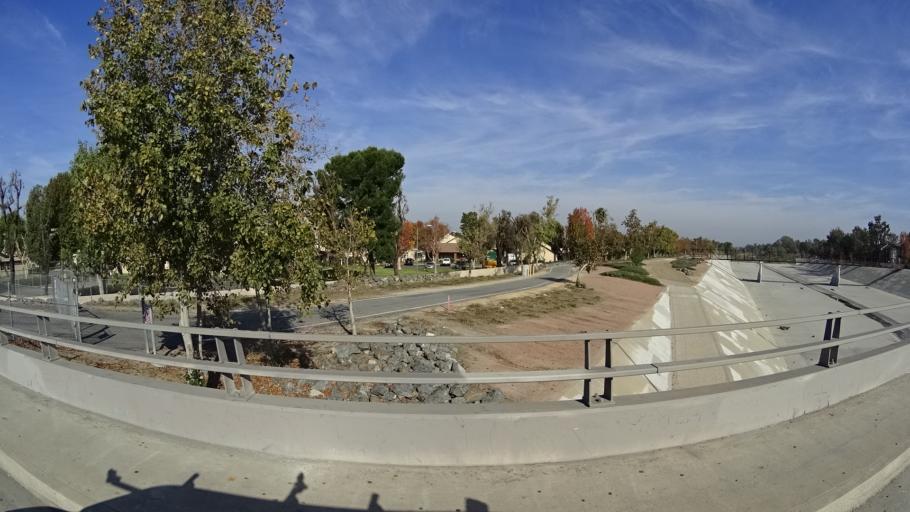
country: US
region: California
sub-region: Orange County
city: Santa Ana
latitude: 33.7600
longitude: -117.9008
